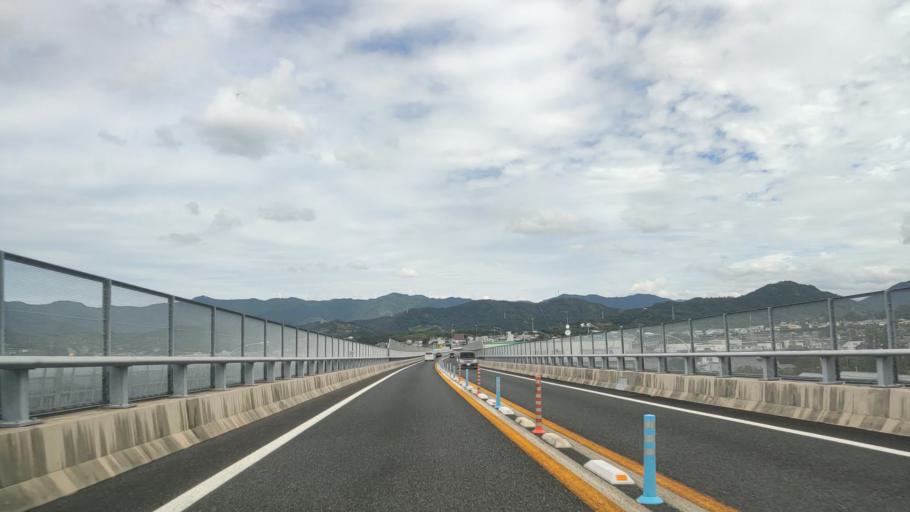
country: JP
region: Wakayama
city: Gobo
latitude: 33.8976
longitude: 135.1844
